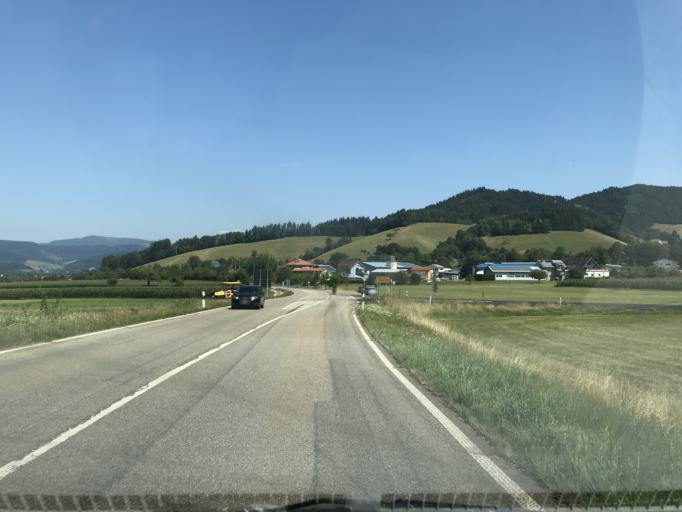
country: DE
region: Baden-Wuerttemberg
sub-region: Freiburg Region
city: Oberried
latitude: 47.9383
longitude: 7.9522
